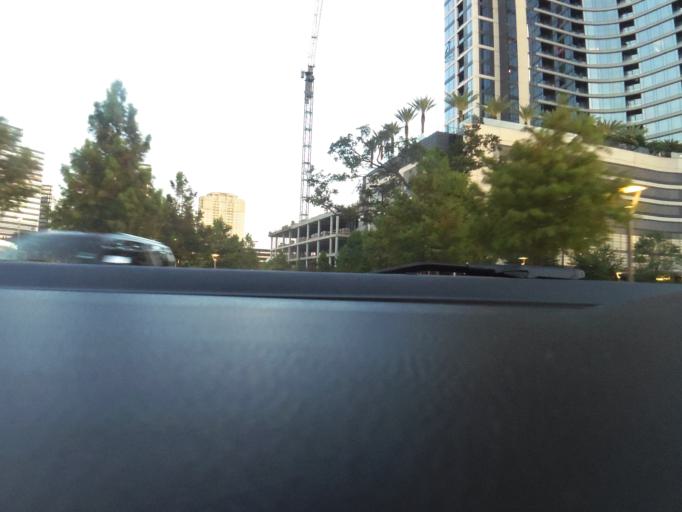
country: US
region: Texas
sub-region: Harris County
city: Hunters Creek Village
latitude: 29.7494
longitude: -95.4631
